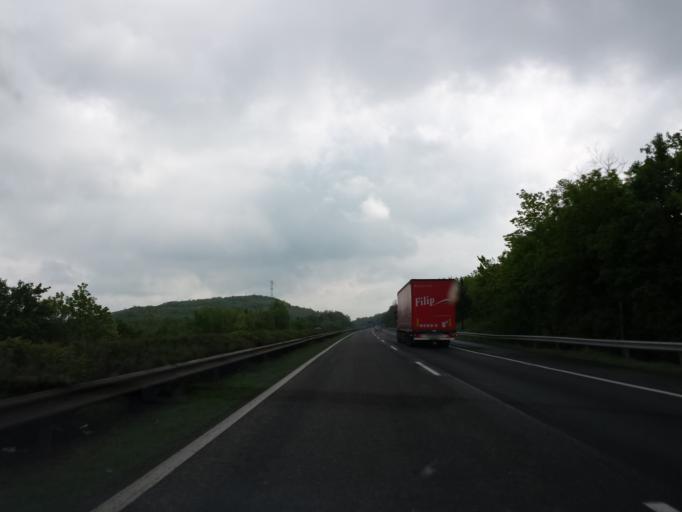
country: HU
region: Fejer
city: Szarliget
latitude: 47.5137
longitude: 18.5340
